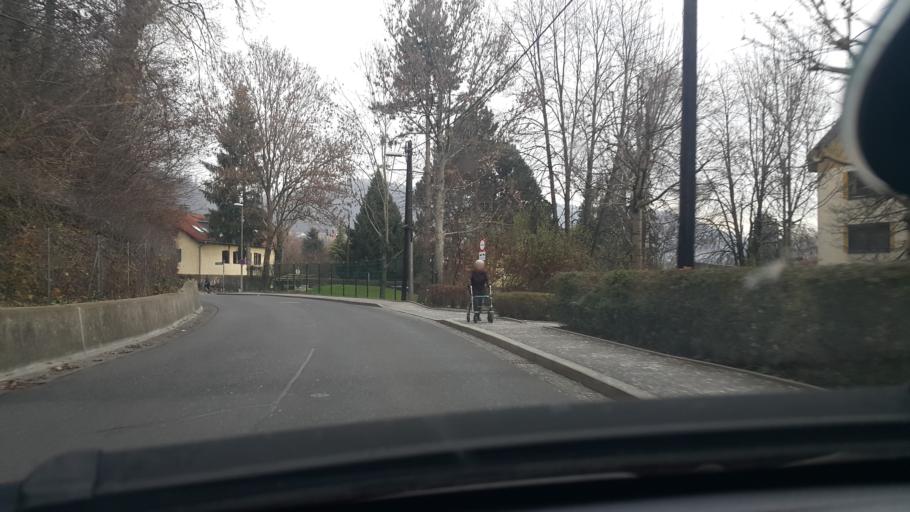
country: AT
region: Styria
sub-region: Graz Stadt
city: Wetzelsdorf
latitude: 47.0526
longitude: 15.3928
